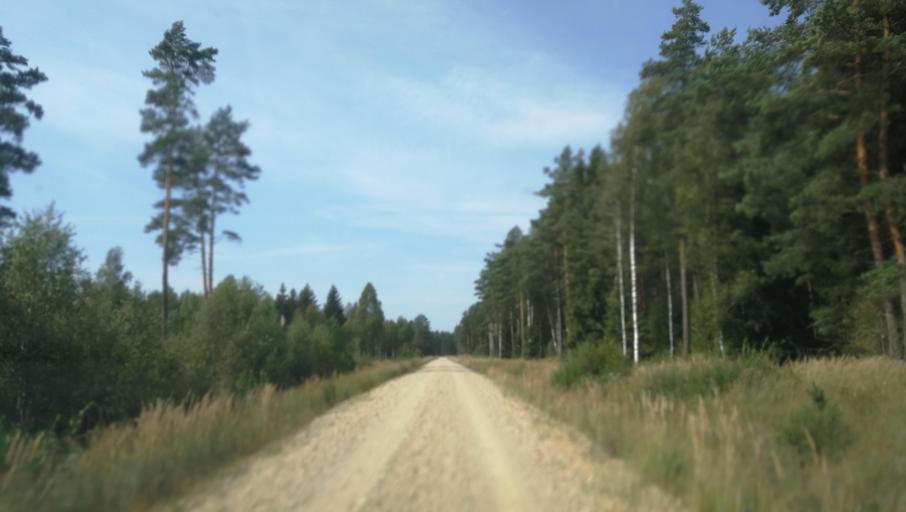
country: LV
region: Pavilostas
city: Pavilosta
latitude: 56.8204
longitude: 21.3010
